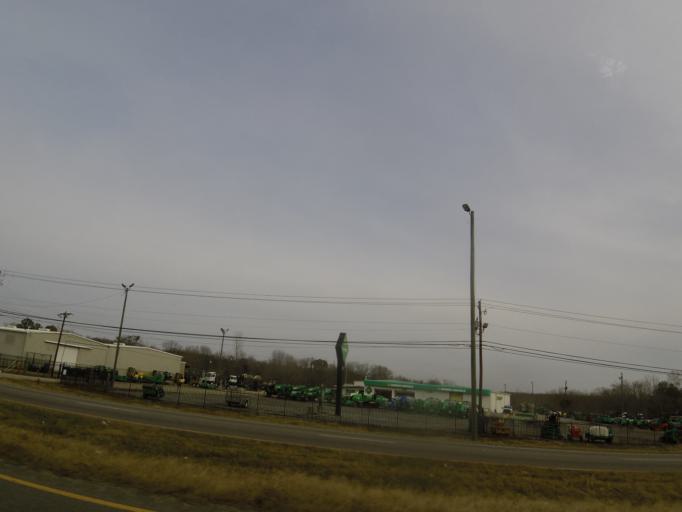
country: US
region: Alabama
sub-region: Montgomery County
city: Montgomery
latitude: 32.3159
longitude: -86.2297
